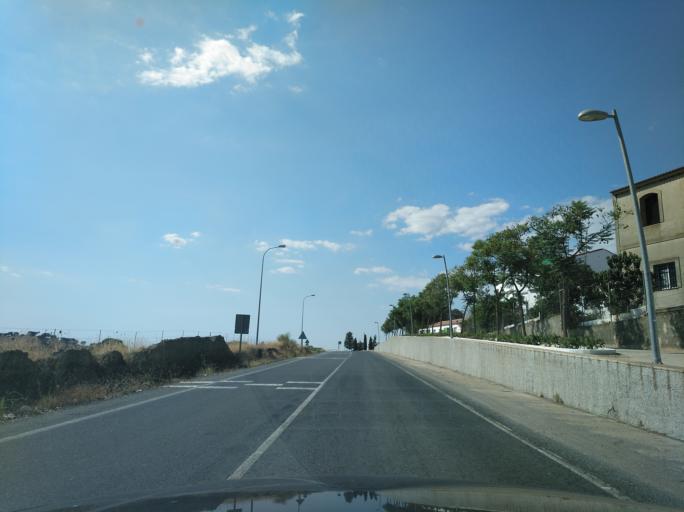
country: ES
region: Andalusia
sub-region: Provincia de Huelva
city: Cabezas Rubias
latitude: 37.7277
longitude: -7.0892
